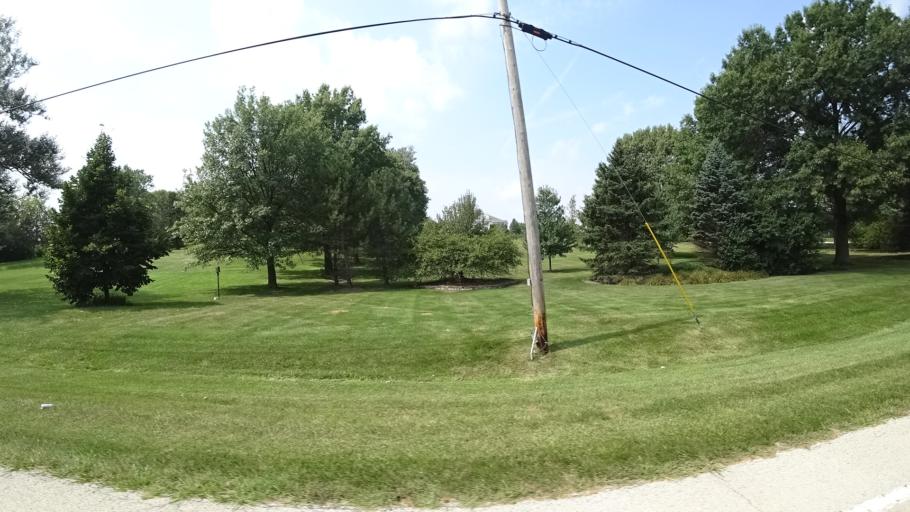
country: US
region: Illinois
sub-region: Cook County
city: Orland Park
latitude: 41.6196
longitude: -87.8824
